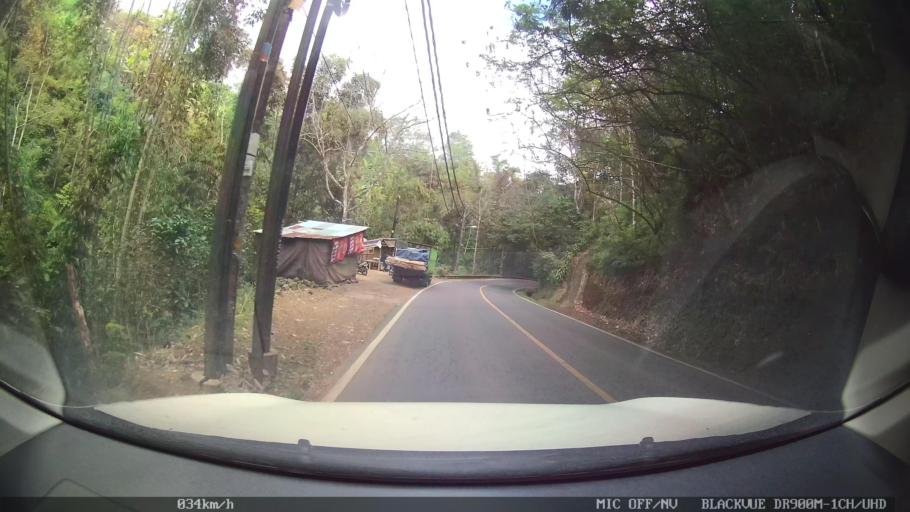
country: ID
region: Bali
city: Banjar Ambengan
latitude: -8.2224
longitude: 115.1478
